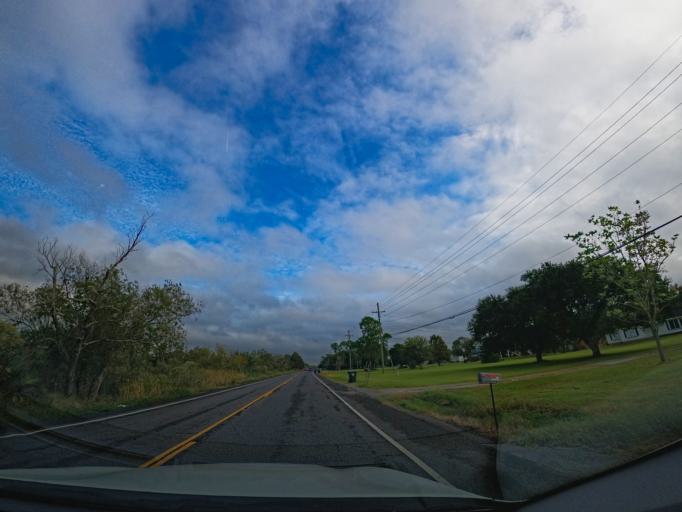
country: US
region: Louisiana
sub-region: Terrebonne Parish
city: Dulac
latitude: 29.4547
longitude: -90.7032
